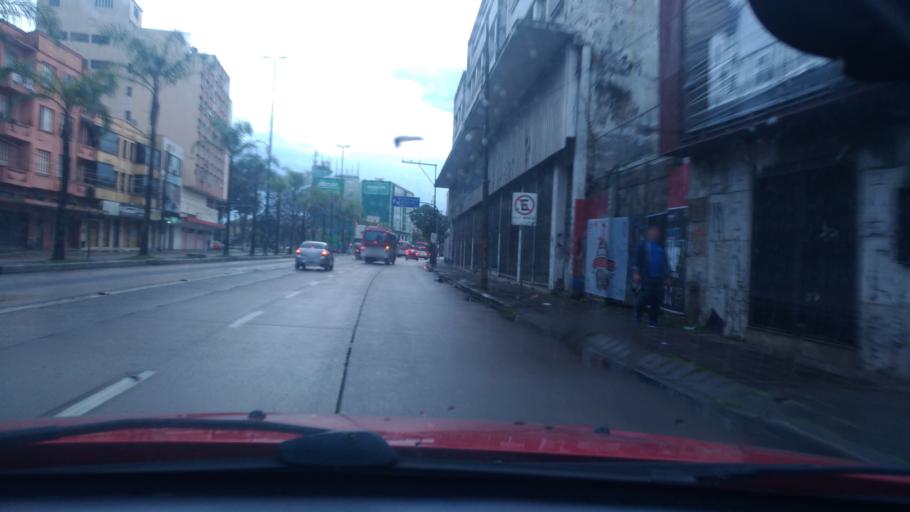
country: BR
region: Rio Grande do Sul
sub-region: Porto Alegre
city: Porto Alegre
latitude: -30.0188
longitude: -51.2095
